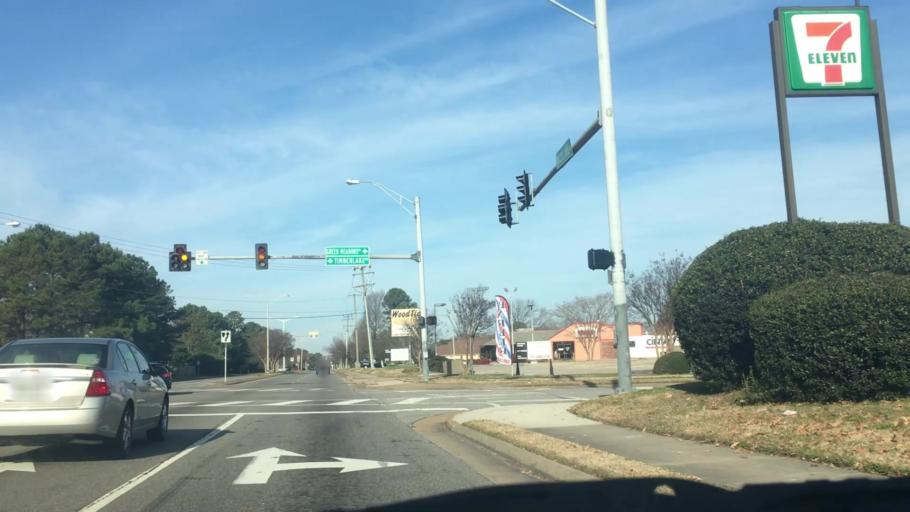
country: US
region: Virginia
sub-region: City of Chesapeake
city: Chesapeake
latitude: 36.8110
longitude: -76.1385
